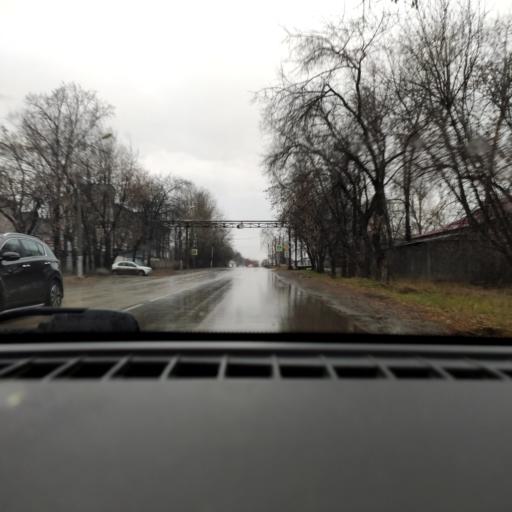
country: RU
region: Perm
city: Kultayevo
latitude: 57.9921
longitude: 55.9312
